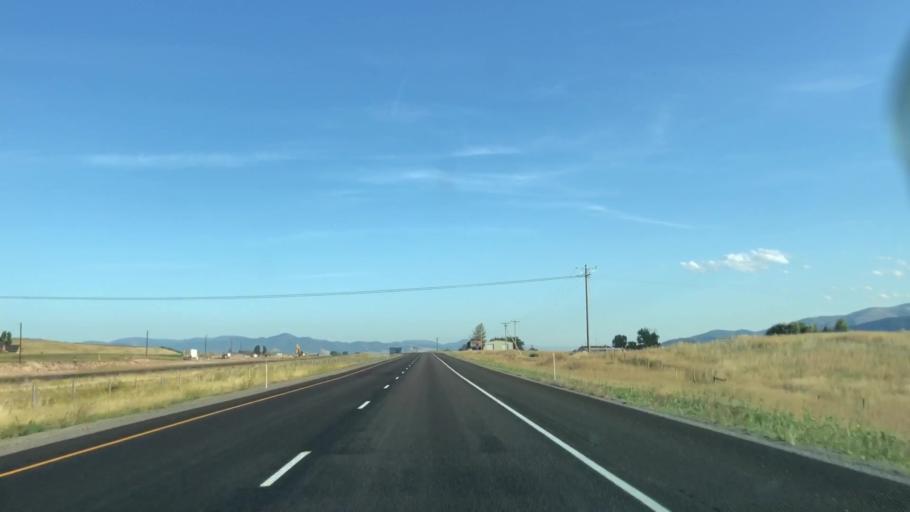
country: US
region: Montana
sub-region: Missoula County
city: Frenchtown
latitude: 46.9756
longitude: -114.1700
